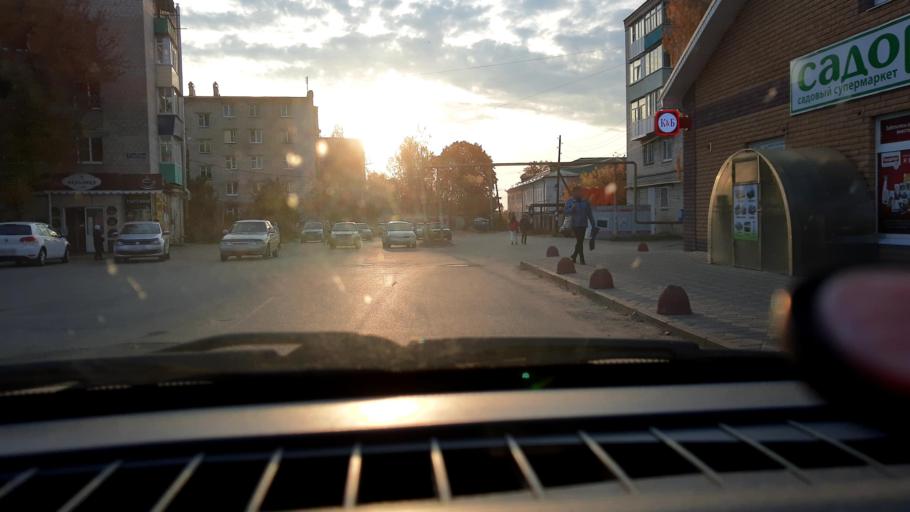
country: RU
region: Nizjnij Novgorod
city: Gorodets
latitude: 56.6464
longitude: 43.4698
